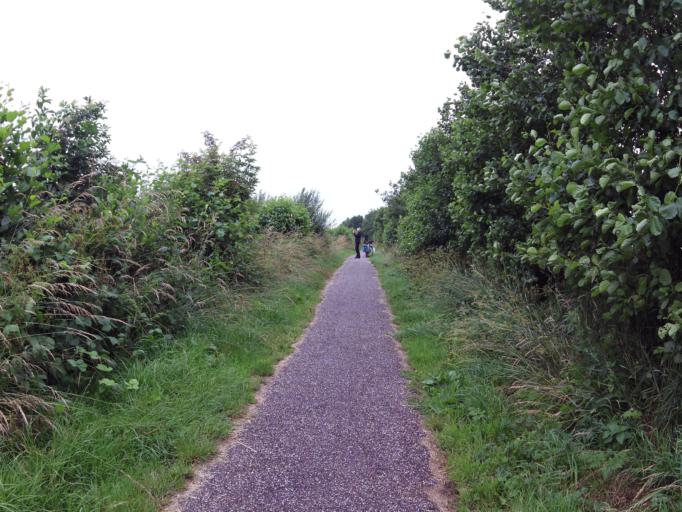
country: NL
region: Utrecht
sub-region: Gemeente Woerden
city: Woerden
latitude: 52.1326
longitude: 4.9396
